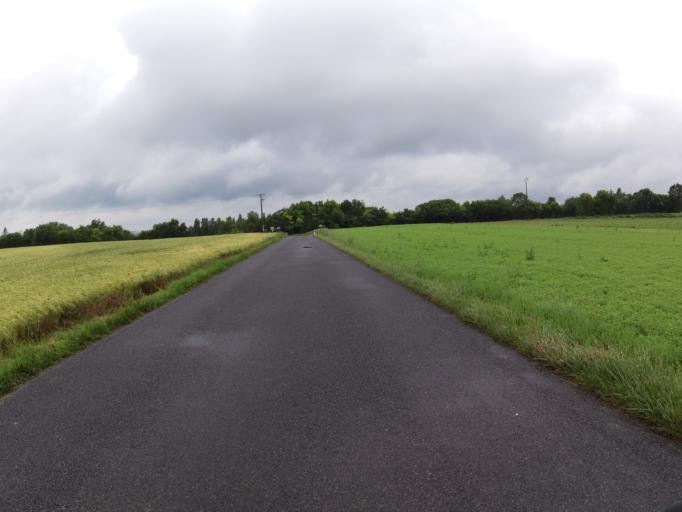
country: FR
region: Poitou-Charentes
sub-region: Departement de la Charente
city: Balzac
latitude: 45.7148
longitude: 0.1297
